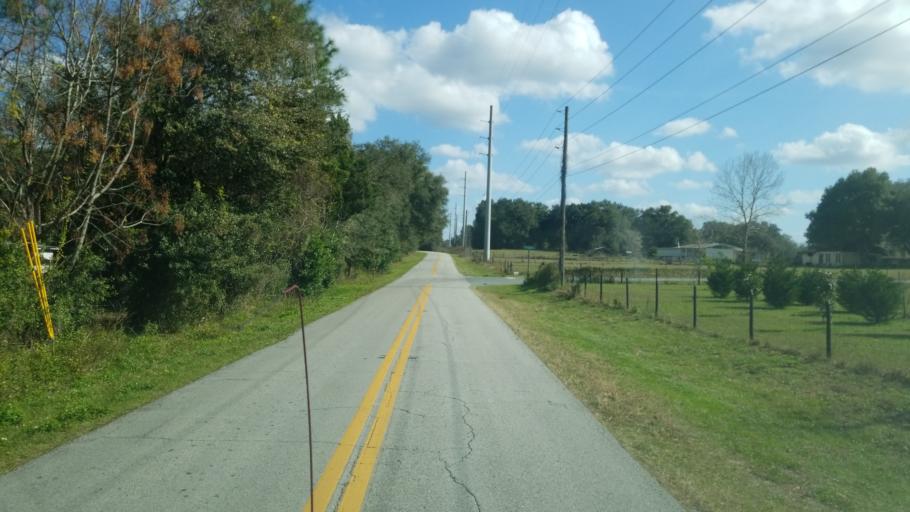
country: US
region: Florida
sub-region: Citrus County
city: Floral City
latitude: 28.7247
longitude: -82.3002
